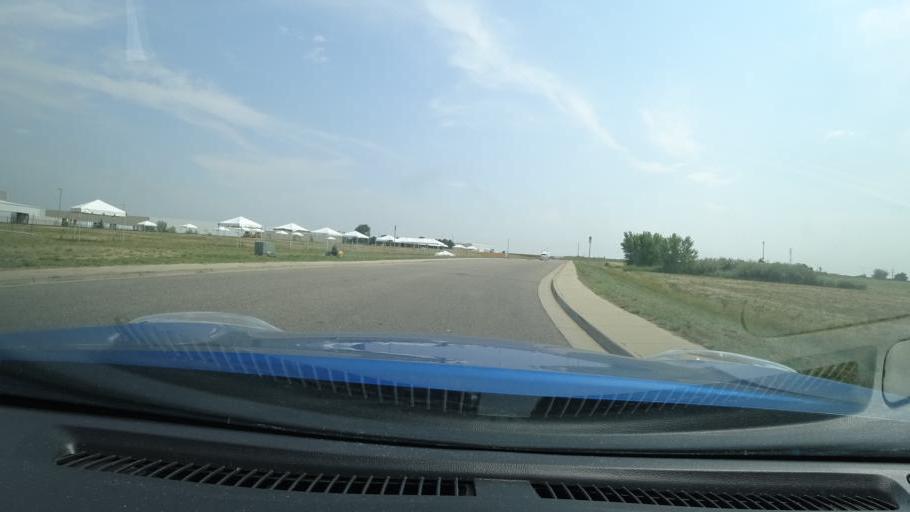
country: US
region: Colorado
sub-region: Adams County
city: Aurora
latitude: 39.7617
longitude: -104.7463
